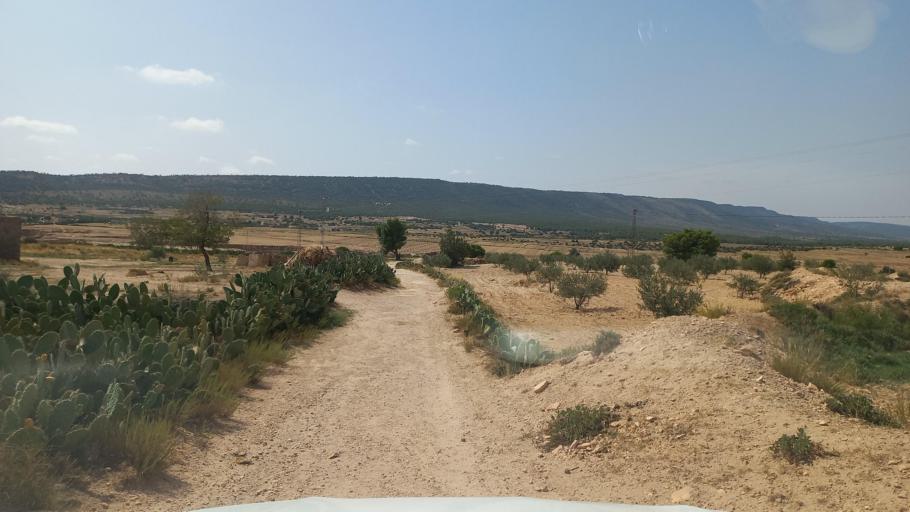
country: TN
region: Al Qasrayn
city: Sbiba
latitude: 35.3959
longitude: 8.9578
